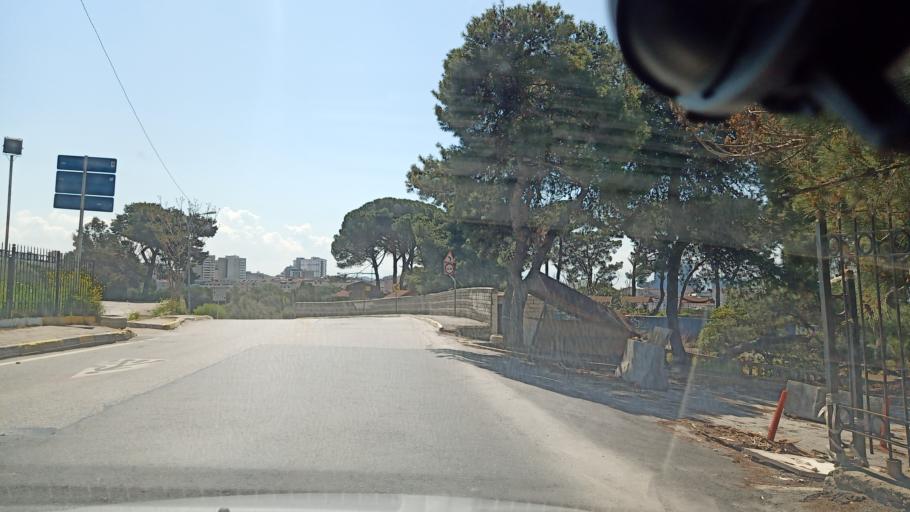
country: TR
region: Istanbul
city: Maltepe
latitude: 40.9491
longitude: 29.1423
